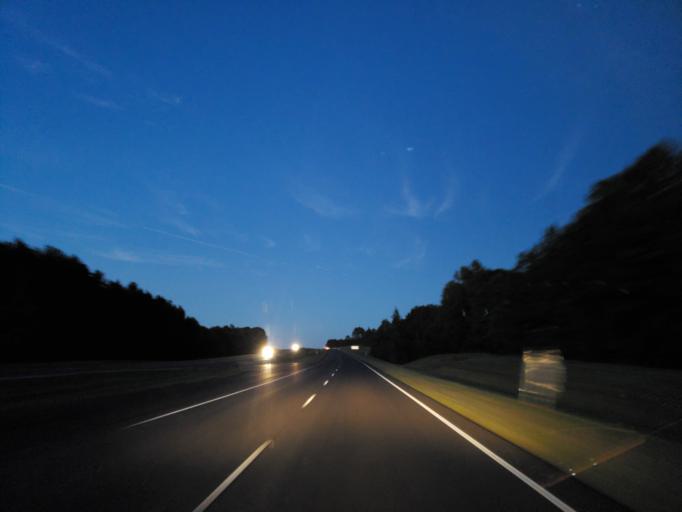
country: US
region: Mississippi
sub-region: Clarke County
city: Quitman
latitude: 32.0022
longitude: -88.6927
